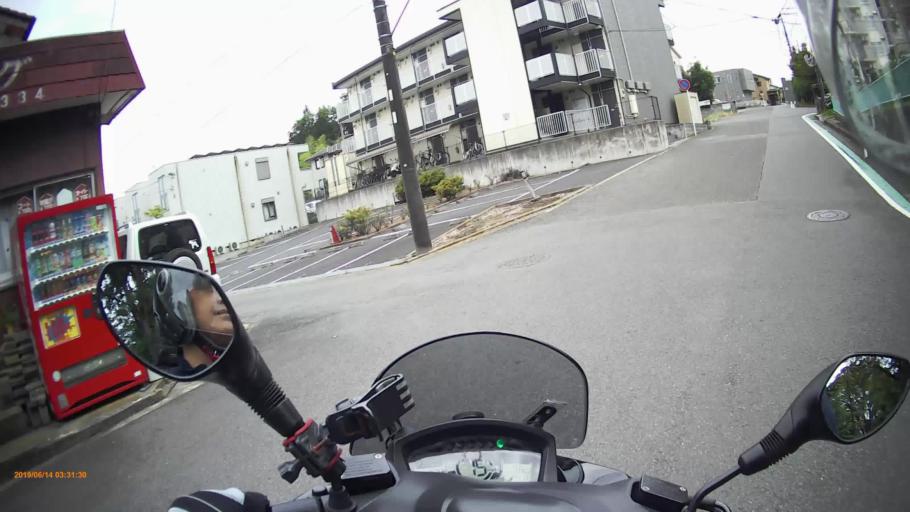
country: JP
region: Kanagawa
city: Minami-rinkan
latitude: 35.4115
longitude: 139.4512
